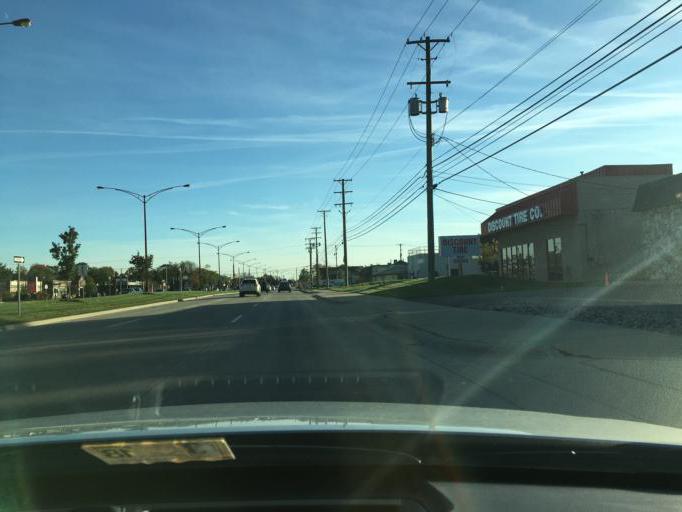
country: US
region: Michigan
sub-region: Oakland County
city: Clawson
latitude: 42.5699
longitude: -83.1282
